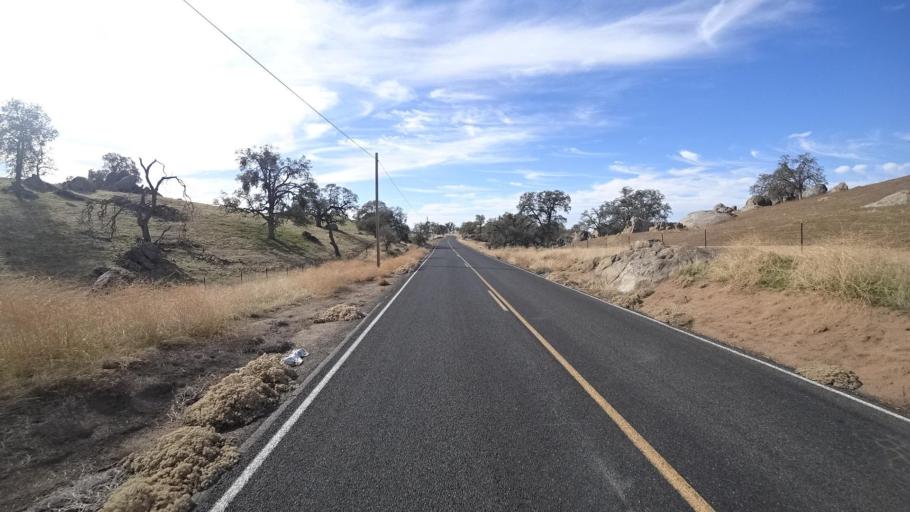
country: US
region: California
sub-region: Kern County
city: Oildale
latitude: 35.6219
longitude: -118.8460
